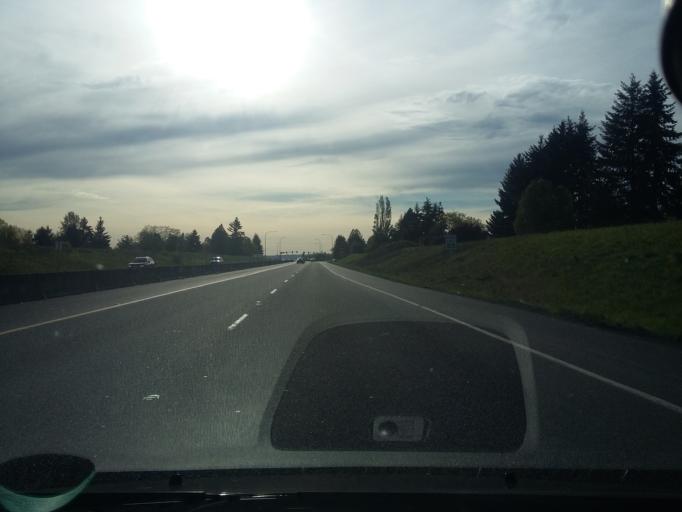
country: US
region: Washington
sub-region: Clark County
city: Walnut Grove
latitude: 45.6480
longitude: -122.6114
